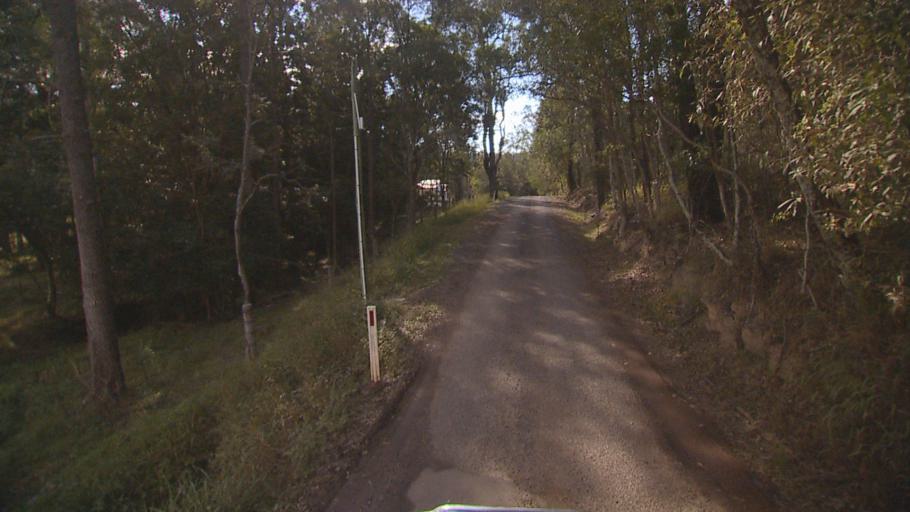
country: AU
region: Queensland
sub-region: Logan
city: Windaroo
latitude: -27.7787
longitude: 153.1739
